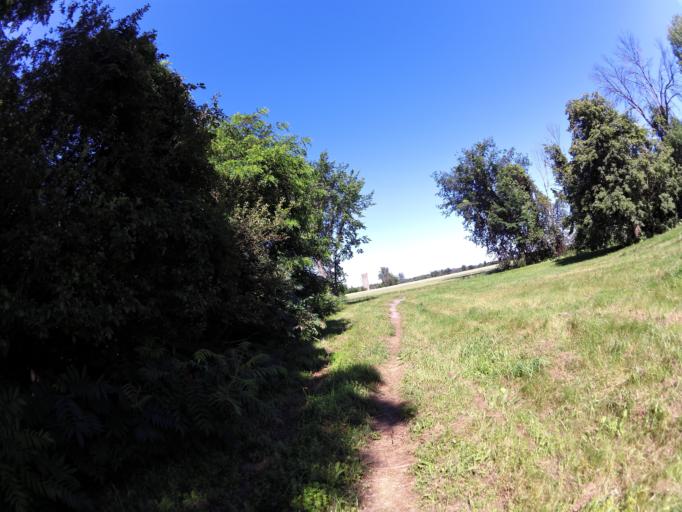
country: CA
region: Ontario
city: Ottawa
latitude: 45.4181
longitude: -75.5926
